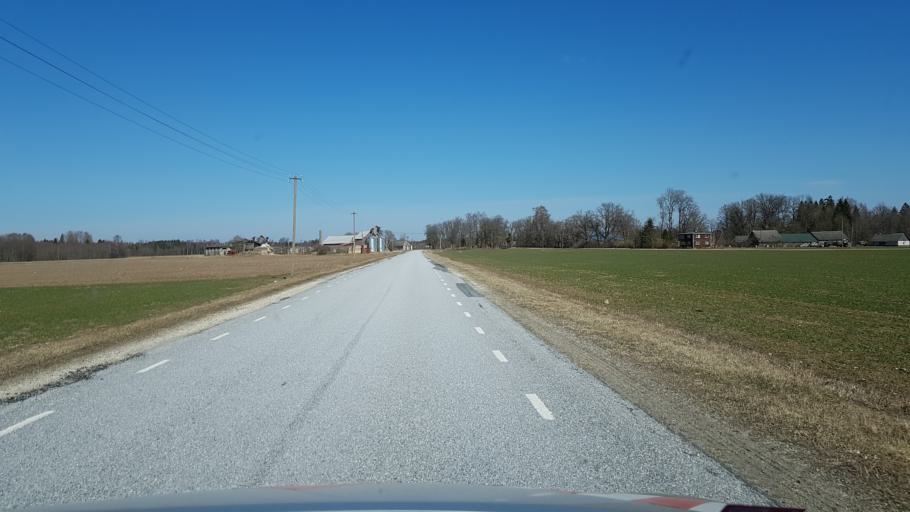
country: EE
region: Laeaene-Virumaa
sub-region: Tamsalu vald
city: Tamsalu
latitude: 59.0644
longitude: 26.1086
